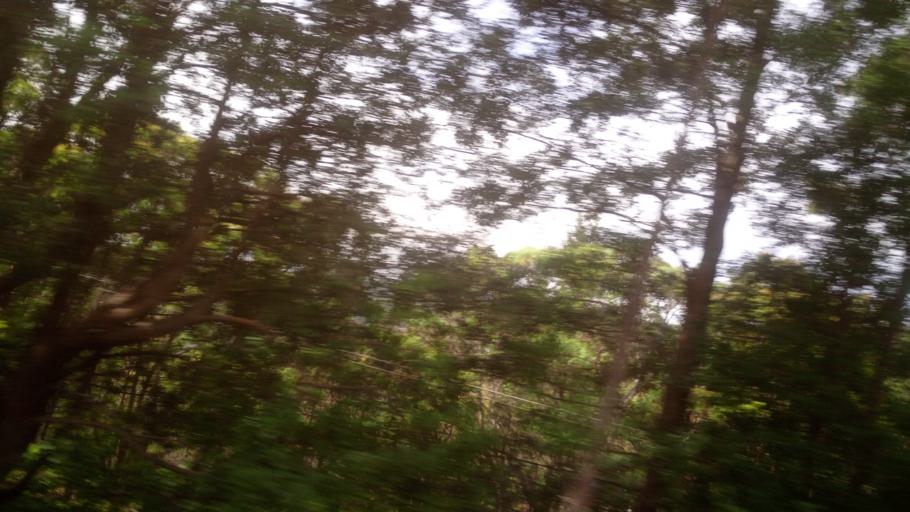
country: AU
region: New South Wales
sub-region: Blue Mountains Municipality
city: Hazelbrook
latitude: -33.7131
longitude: 150.5180
